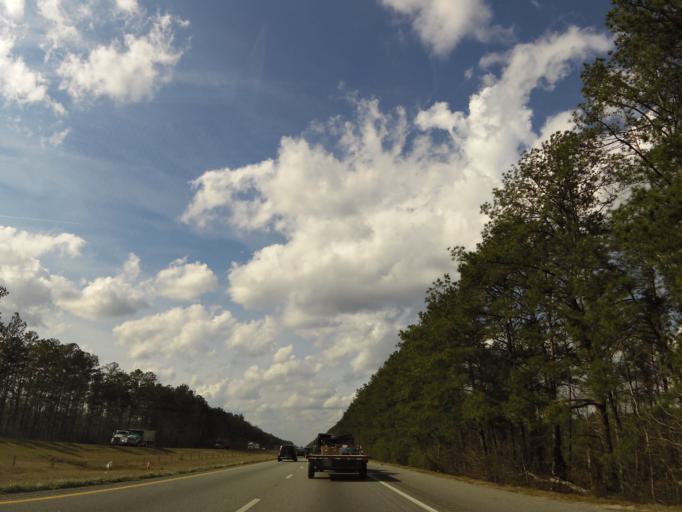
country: US
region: South Carolina
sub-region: Dorchester County
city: Ridgeville
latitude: 33.1207
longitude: -80.2760
